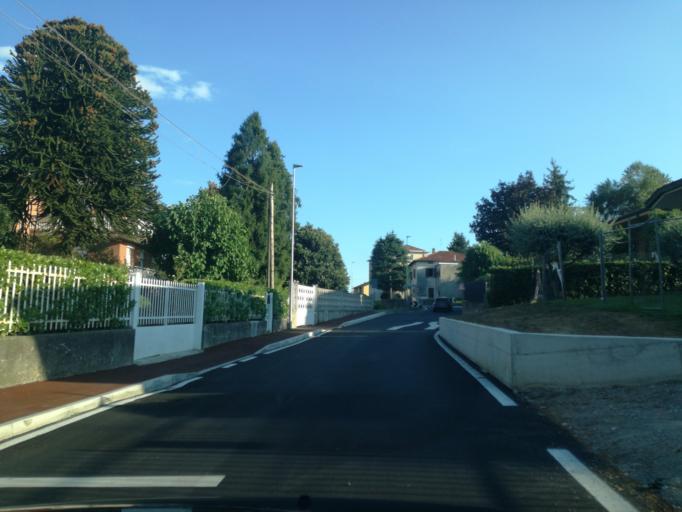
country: IT
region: Lombardy
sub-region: Provincia di Lecco
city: Paderno d'Adda
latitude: 45.6806
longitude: 9.4470
